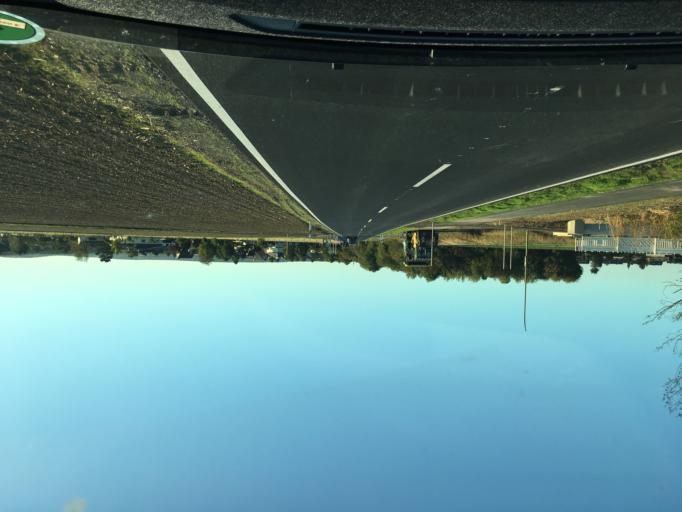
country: DE
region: North Rhine-Westphalia
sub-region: Regierungsbezirk Koln
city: Langerwehe
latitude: 50.8060
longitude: 6.3956
